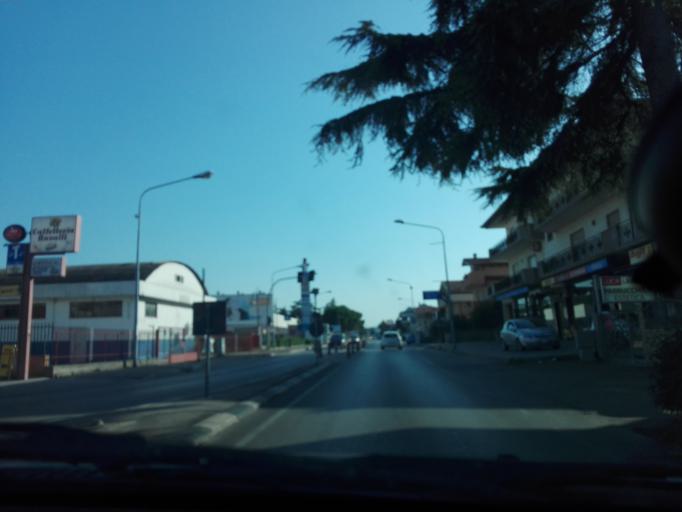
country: IT
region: Abruzzo
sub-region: Provincia di Pescara
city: Montesilvano Marina
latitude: 42.5021
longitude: 14.1343
